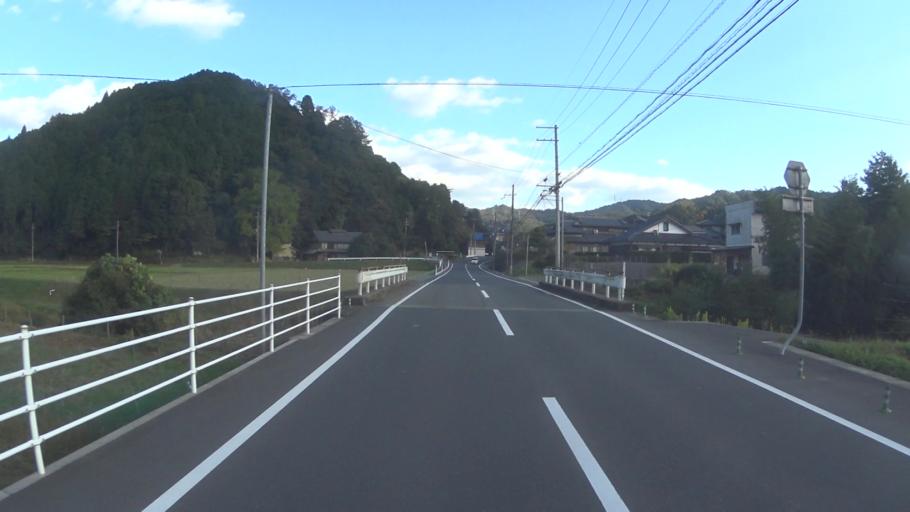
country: JP
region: Kyoto
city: Maizuru
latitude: 35.4311
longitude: 135.2303
